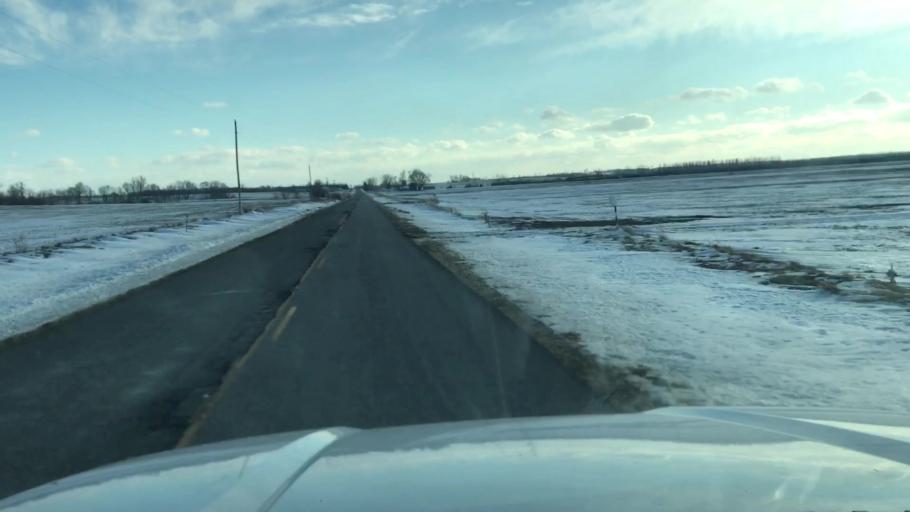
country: US
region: Missouri
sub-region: Holt County
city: Oregon
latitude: 40.1253
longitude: -95.0225
